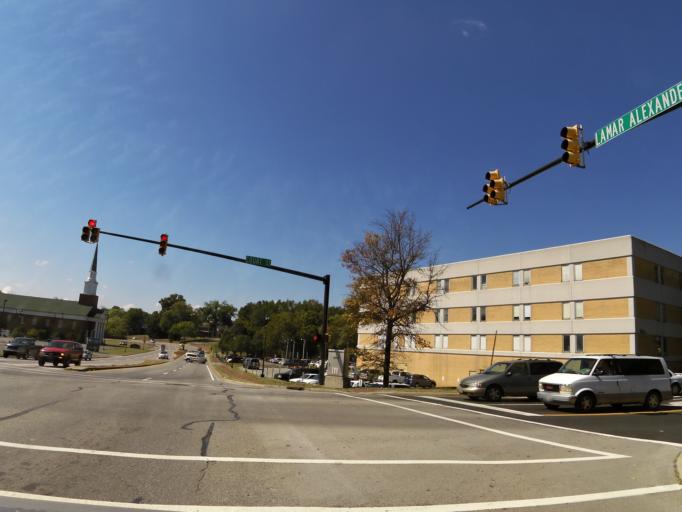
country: US
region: Tennessee
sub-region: Blount County
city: Maryville
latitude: 35.7541
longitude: -83.9684
